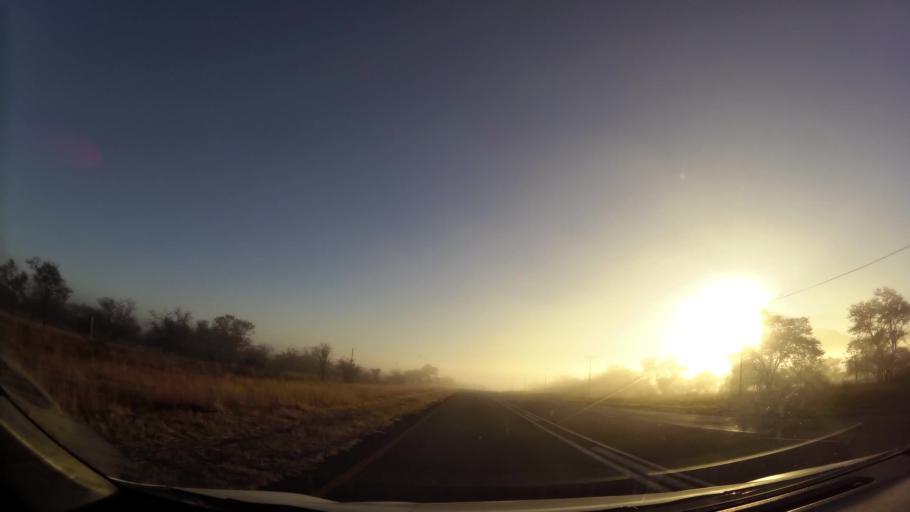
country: ZA
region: Limpopo
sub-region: Capricorn District Municipality
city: Polokwane
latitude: -24.0377
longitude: 29.2817
